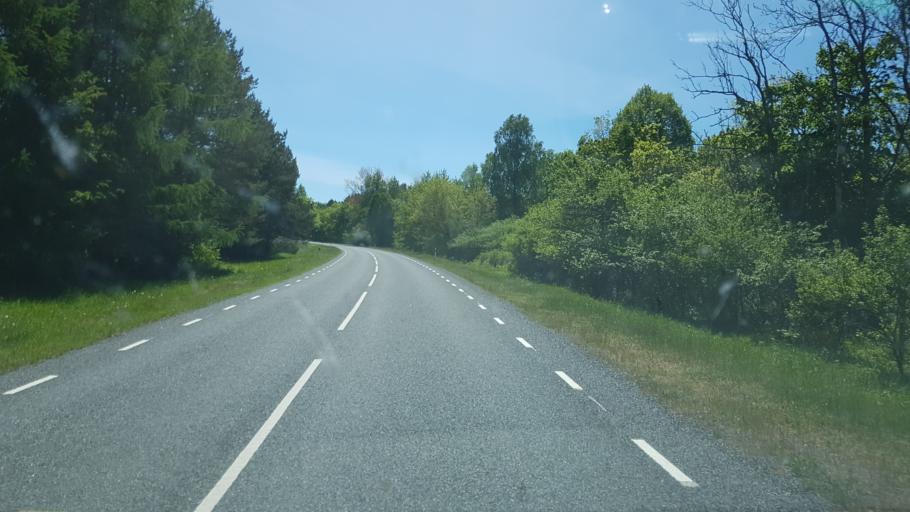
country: EE
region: Saare
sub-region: Kuressaare linn
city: Kuressaare
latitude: 58.0653
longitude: 22.2061
